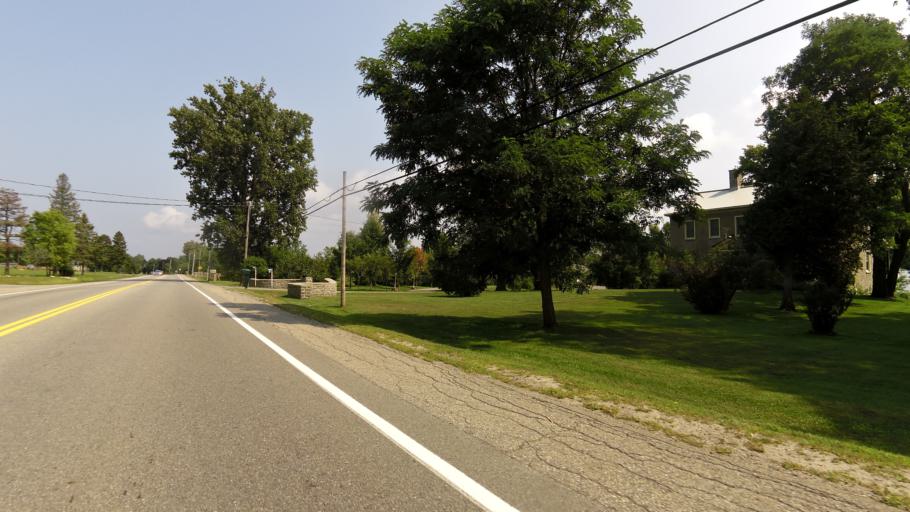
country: CA
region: Ontario
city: Brockville
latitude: 44.6247
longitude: -75.6297
